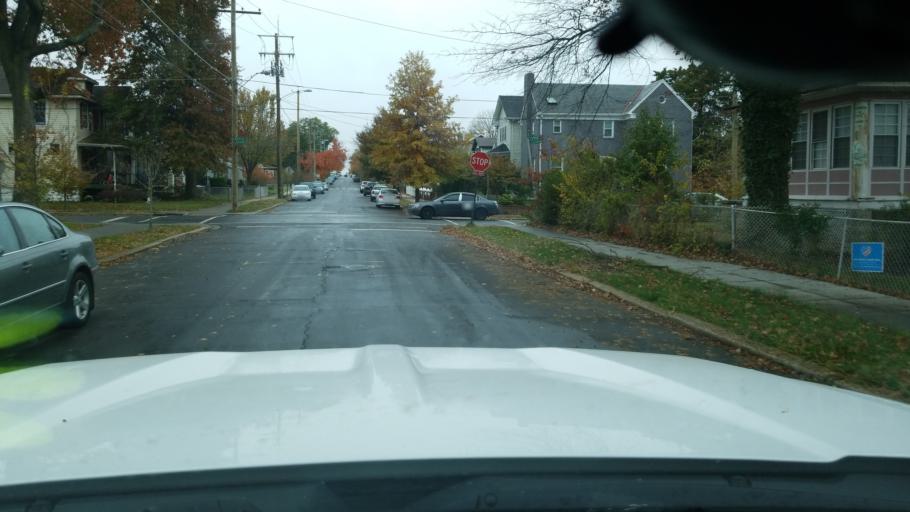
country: US
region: Maryland
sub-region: Prince George's County
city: Mount Rainier
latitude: 38.9354
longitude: -76.9722
